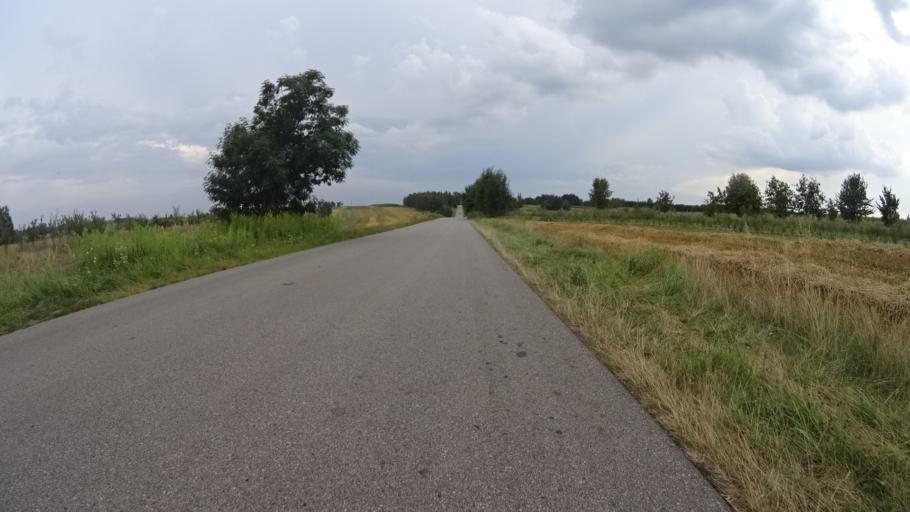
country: PL
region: Masovian Voivodeship
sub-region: Powiat grojecki
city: Goszczyn
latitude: 51.6741
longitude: 20.8582
